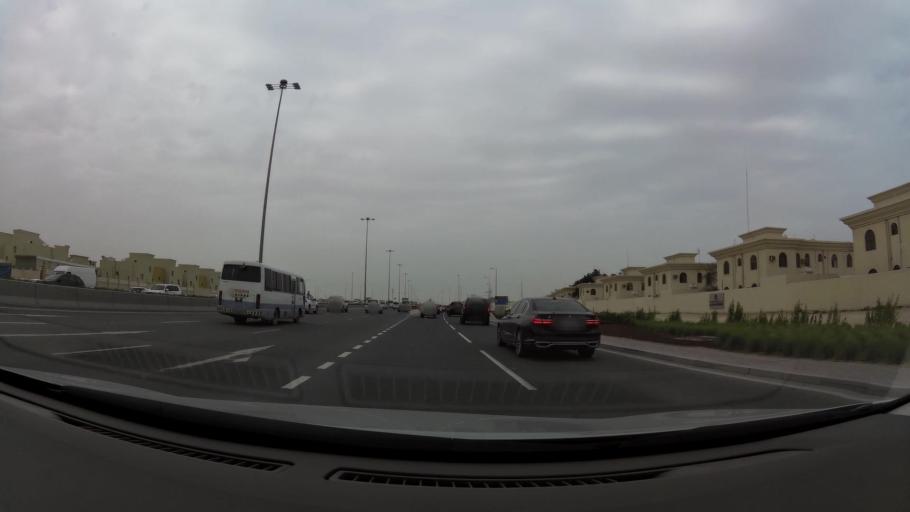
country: QA
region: Baladiyat ar Rayyan
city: Ar Rayyan
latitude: 25.3413
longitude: 51.4598
